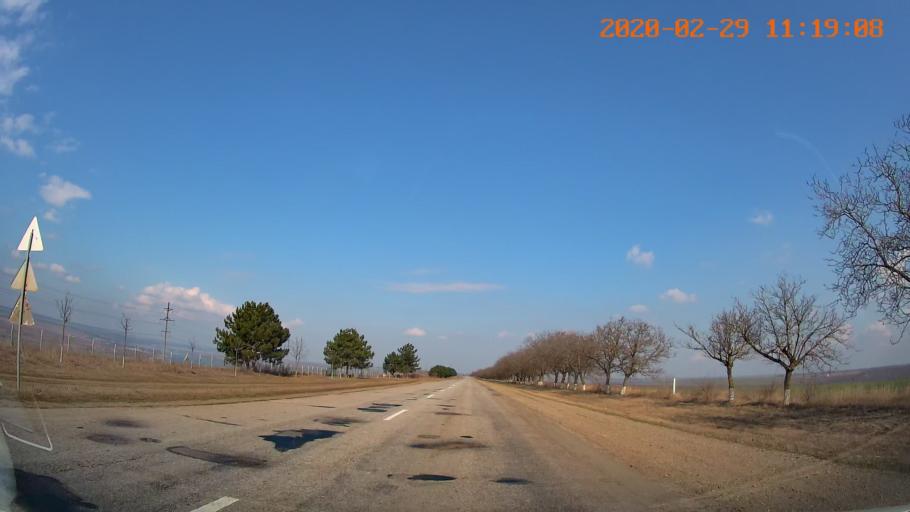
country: MD
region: Telenesti
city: Cocieri
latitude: 47.3452
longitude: 29.1757
